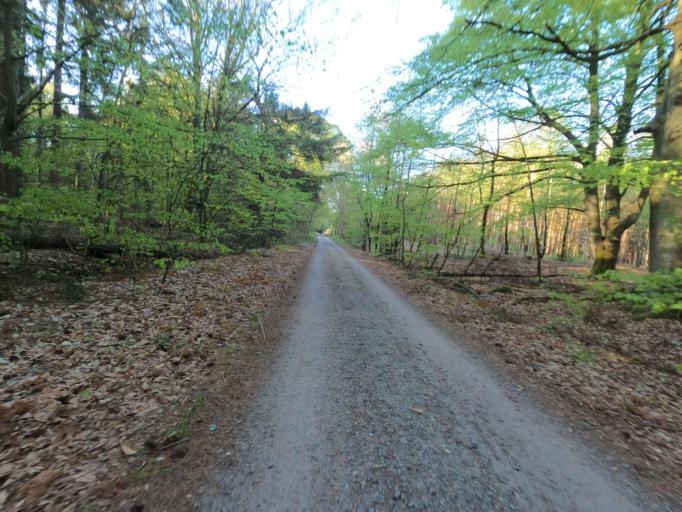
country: DE
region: Mecklenburg-Vorpommern
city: Born
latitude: 54.4269
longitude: 12.5373
